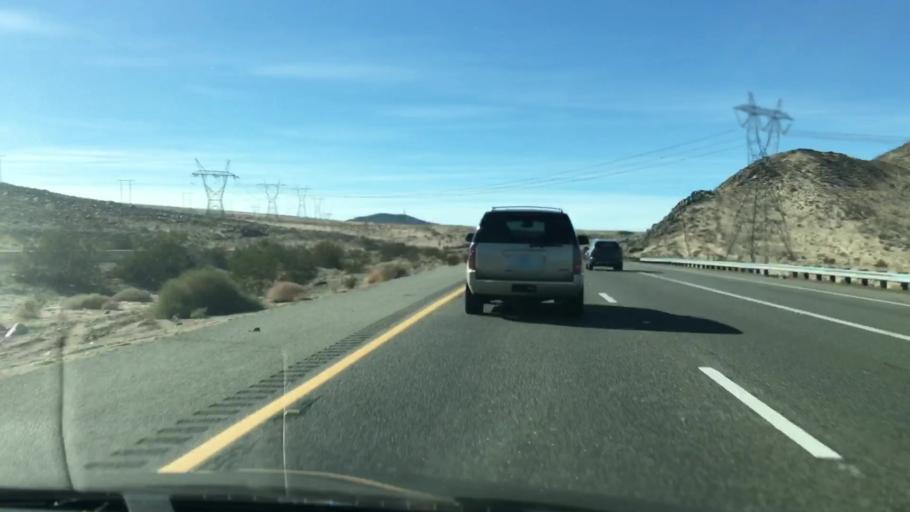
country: US
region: California
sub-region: San Bernardino County
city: Fort Irwin
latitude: 35.0857
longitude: -116.3210
